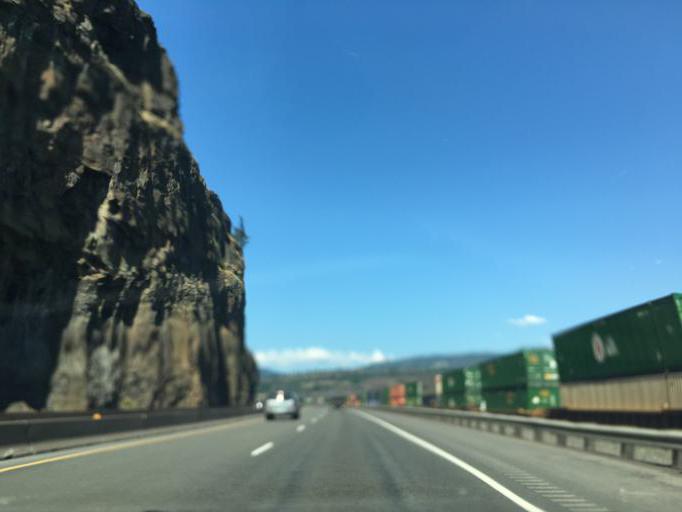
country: US
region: Oregon
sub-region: Wasco County
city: Chenoweth
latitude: 45.6901
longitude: -121.3015
